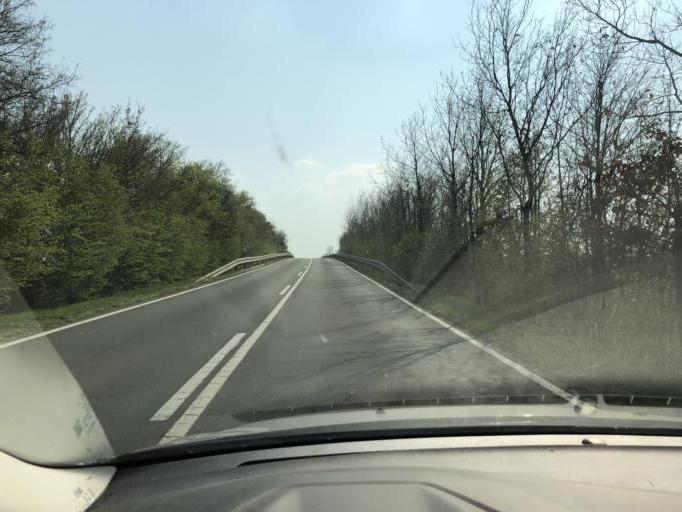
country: DE
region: Saxony-Anhalt
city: Grobers
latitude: 51.4533
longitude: 12.1186
